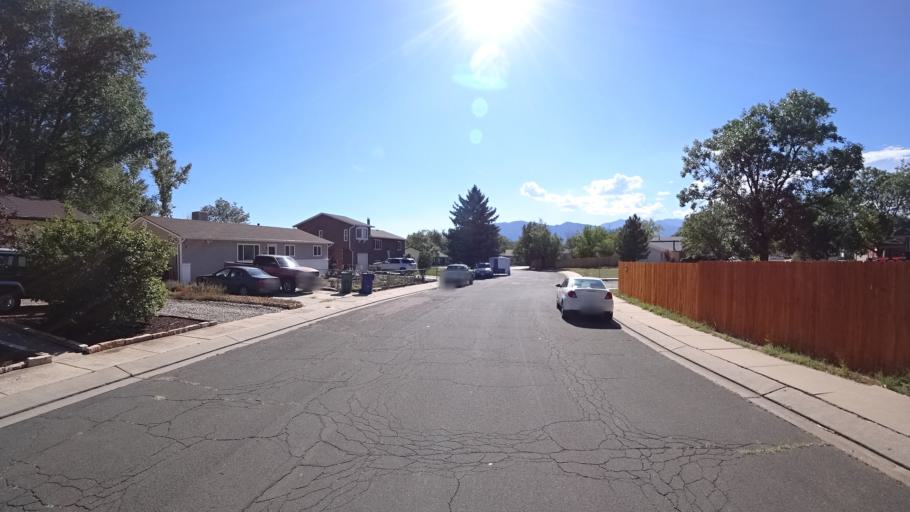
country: US
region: Colorado
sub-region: El Paso County
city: Stratmoor
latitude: 38.7997
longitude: -104.7472
